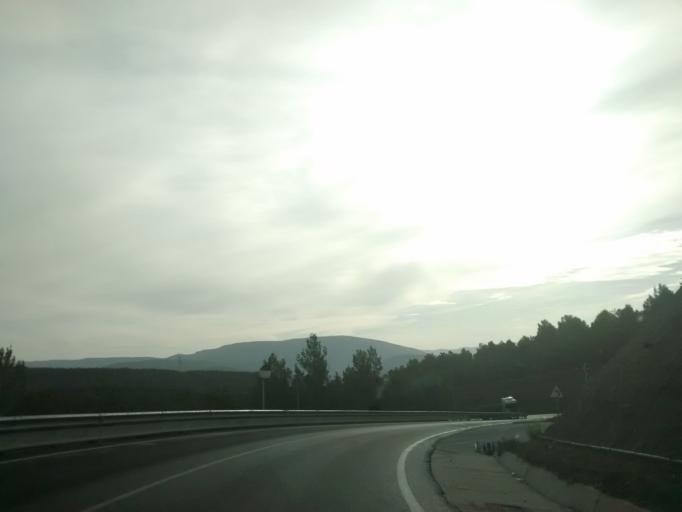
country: ES
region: Aragon
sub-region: Provincia de Zaragoza
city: Undues de Lerda
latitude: 42.6205
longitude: -1.1151
